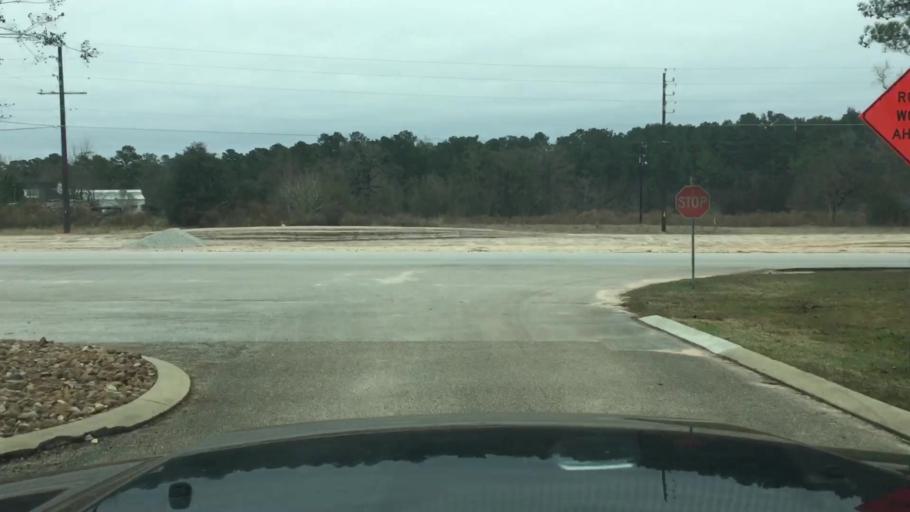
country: US
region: Texas
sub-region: Montgomery County
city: Panorama Village
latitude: 30.3360
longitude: -95.5872
